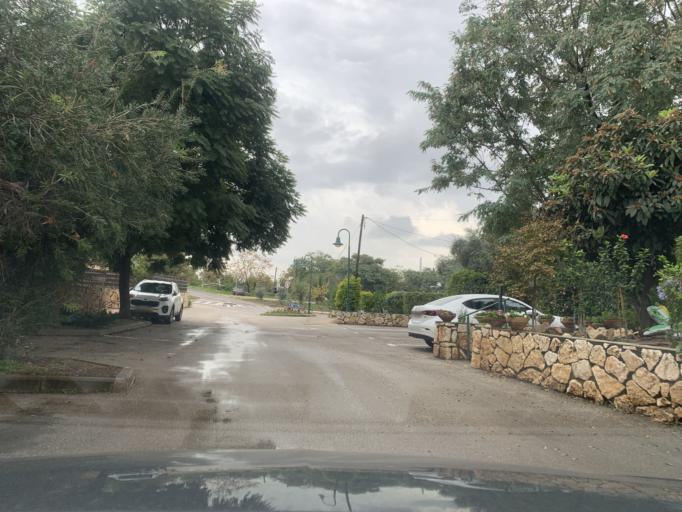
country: PS
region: West Bank
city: Qalqilyah
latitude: 32.2120
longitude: 34.9812
